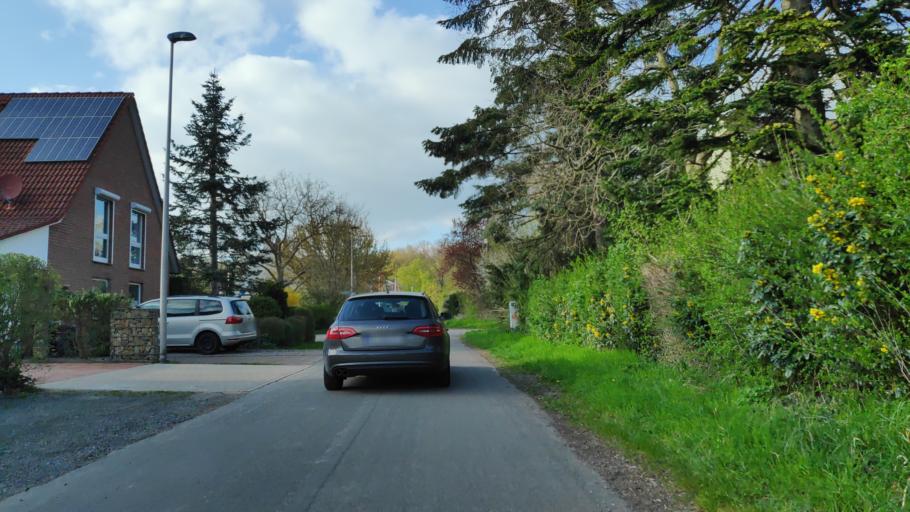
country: DE
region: North Rhine-Westphalia
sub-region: Regierungsbezirk Detmold
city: Minden
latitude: 52.2782
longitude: 8.9159
